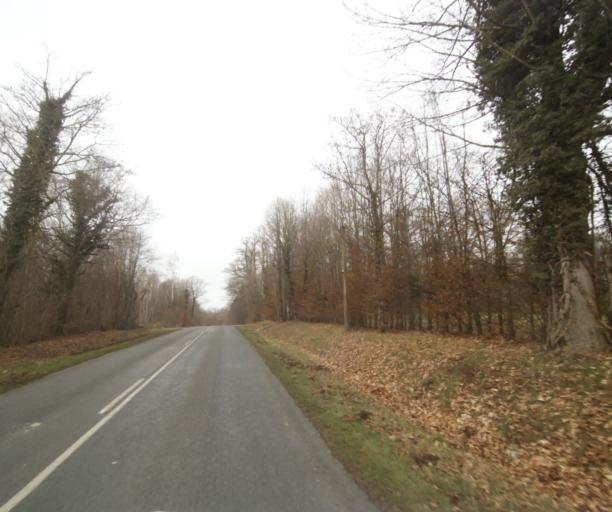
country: FR
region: Champagne-Ardenne
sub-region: Departement de la Haute-Marne
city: Villiers-en-Lieu
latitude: 48.7058
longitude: 4.8922
